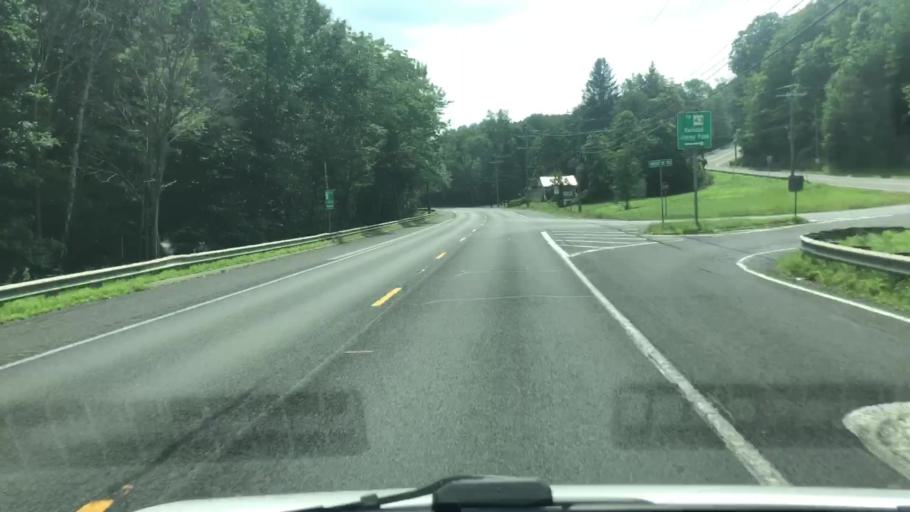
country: US
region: Massachusetts
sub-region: Berkshire County
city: Lanesborough
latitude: 42.5744
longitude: -73.2495
